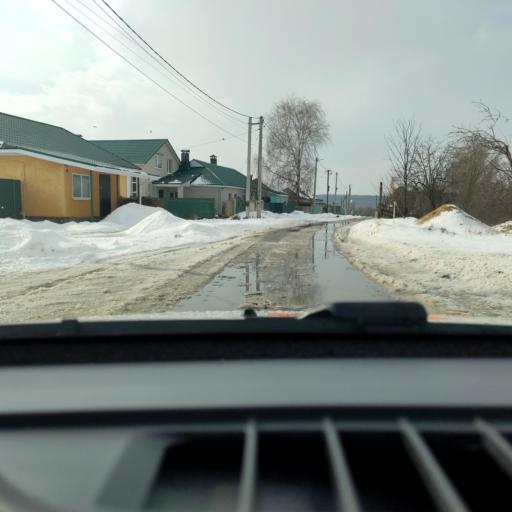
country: RU
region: Voronezj
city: Podgornoye
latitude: 51.7688
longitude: 39.1115
